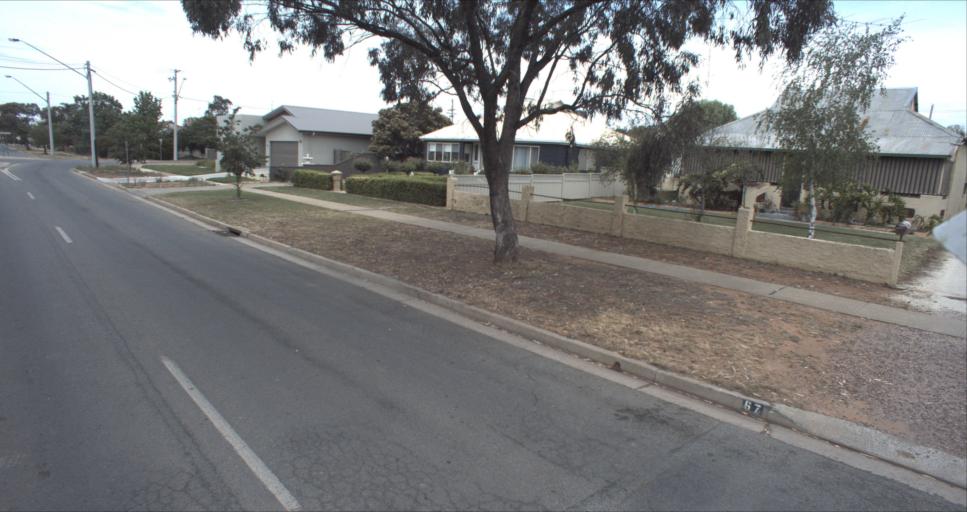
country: AU
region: New South Wales
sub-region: Leeton
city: Leeton
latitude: -34.5489
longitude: 146.4115
